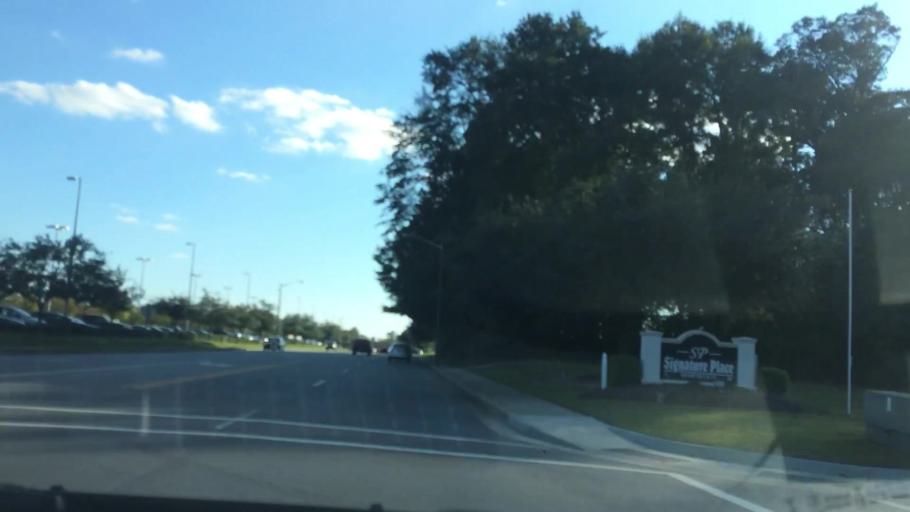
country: US
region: North Carolina
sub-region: Pitt County
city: Summerfield
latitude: 35.6089
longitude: -77.4106
